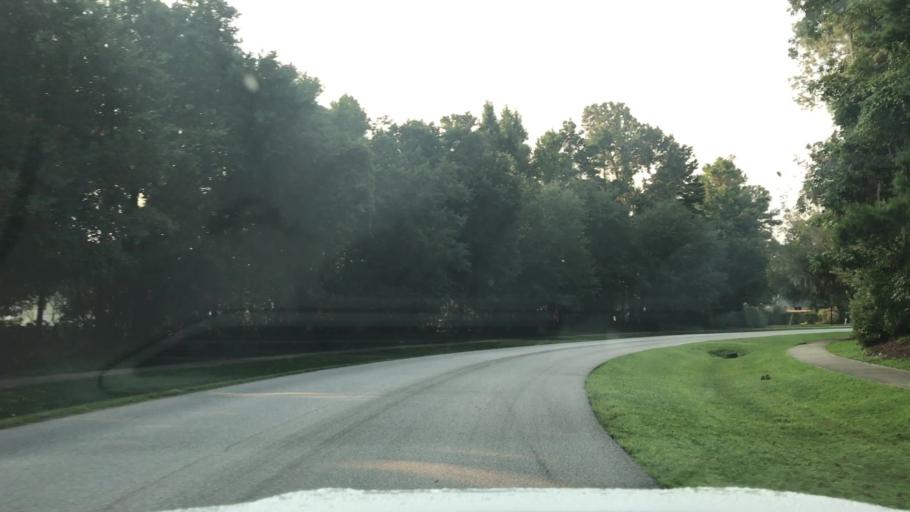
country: US
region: South Carolina
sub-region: Charleston County
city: Shell Point
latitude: 32.8406
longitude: -80.0869
